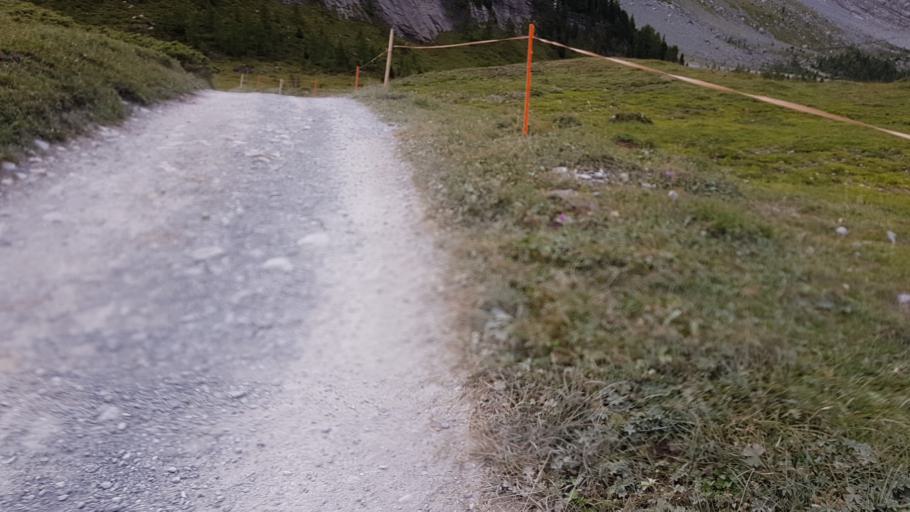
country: CH
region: Bern
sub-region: Frutigen-Niedersimmental District
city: Kandersteg
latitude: 46.4467
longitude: 7.6437
